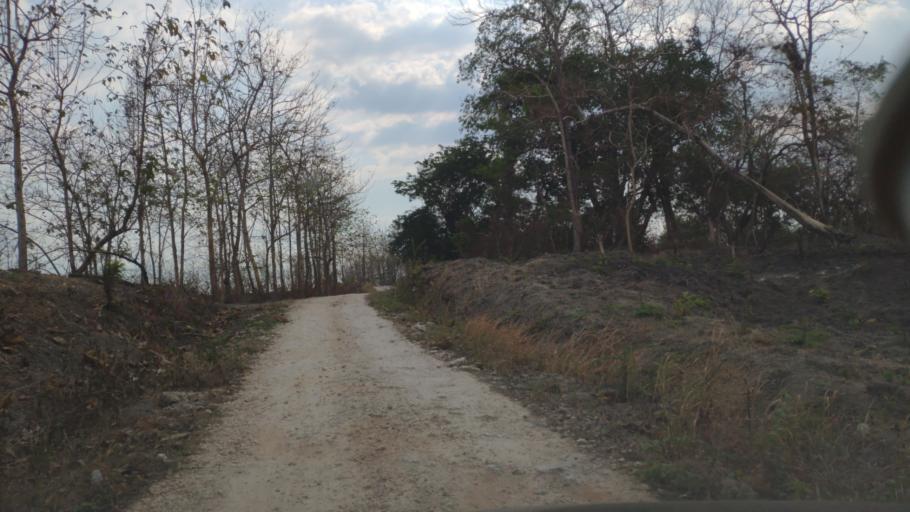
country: ID
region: Central Java
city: Randublatung
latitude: -7.3023
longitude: 111.3413
